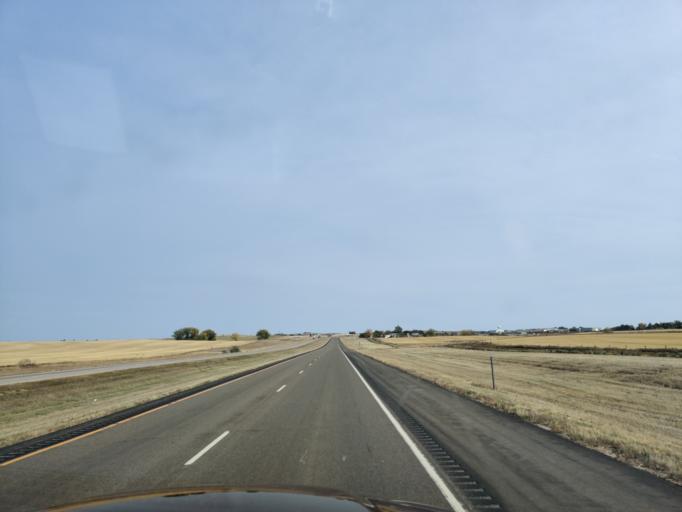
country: US
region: North Dakota
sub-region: Stark County
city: Dickinson
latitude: 46.8935
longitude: -102.7602
